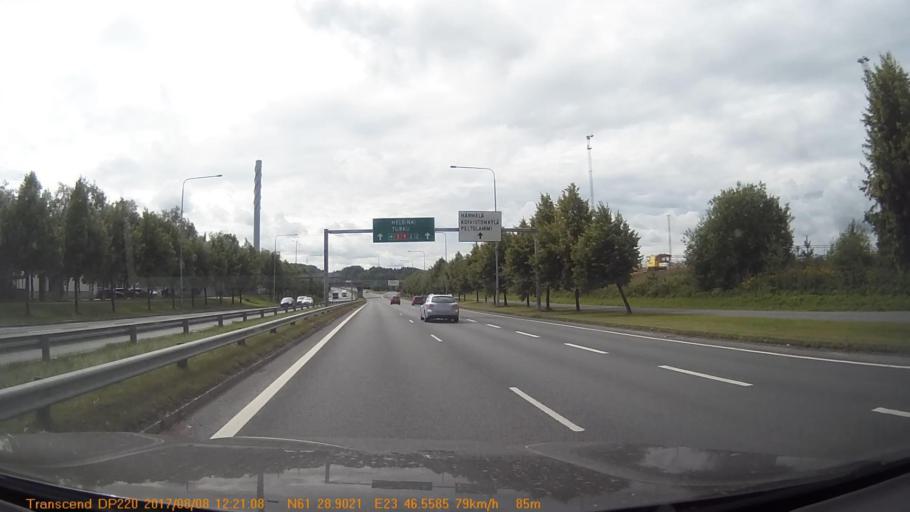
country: FI
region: Pirkanmaa
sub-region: Tampere
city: Tampere
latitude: 61.4812
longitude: 23.7758
